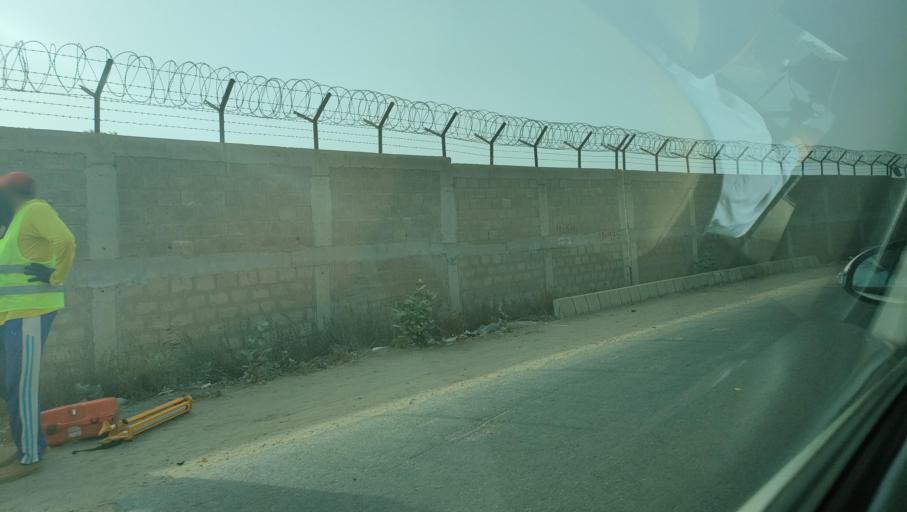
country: PK
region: Sindh
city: Malir Cantonment
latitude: 24.9142
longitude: 67.1884
